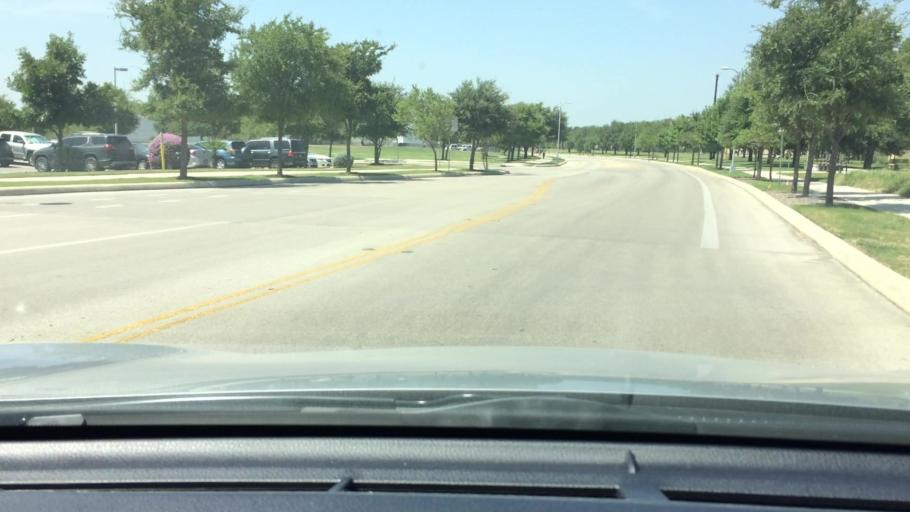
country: US
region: Texas
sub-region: Bexar County
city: San Antonio
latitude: 29.3440
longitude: -98.4437
